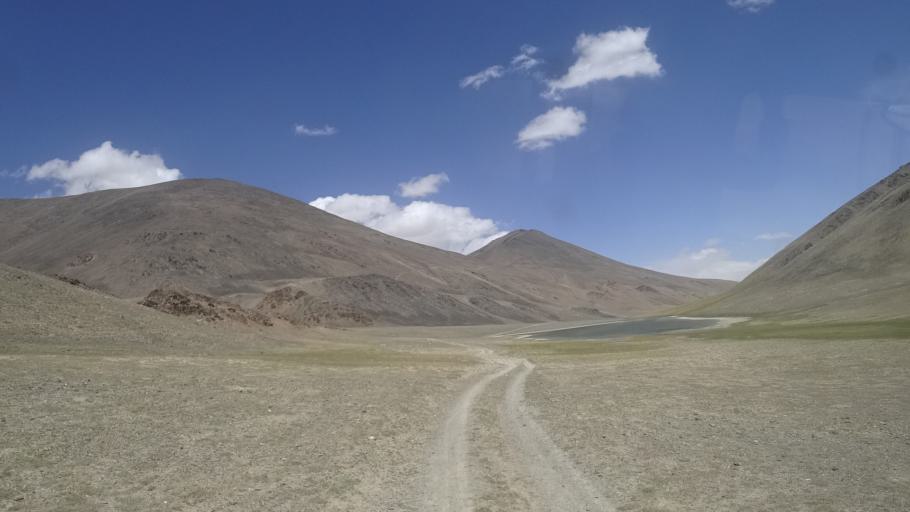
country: TJ
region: Gorno-Badakhshan
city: Murghob
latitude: 37.5194
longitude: 74.0598
